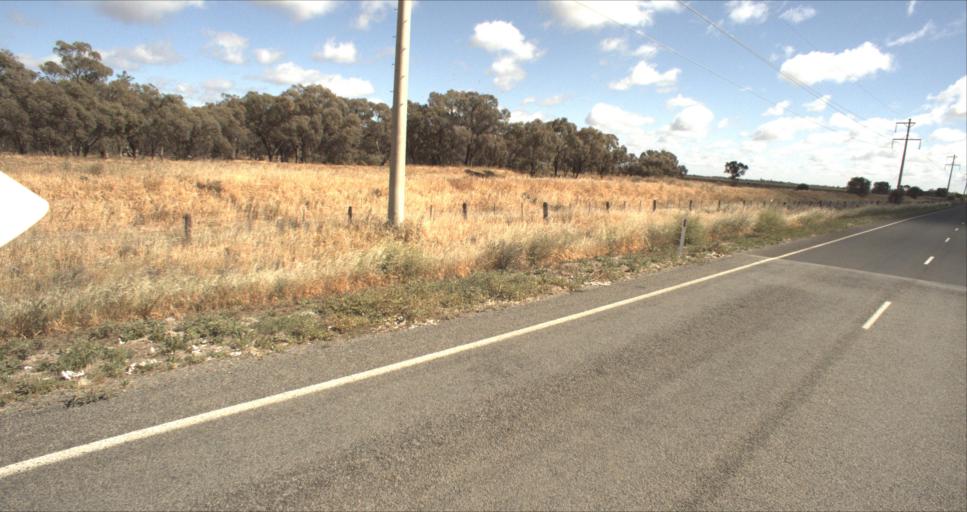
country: AU
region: New South Wales
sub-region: Murrumbidgee Shire
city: Darlington Point
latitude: -34.5442
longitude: 146.1716
